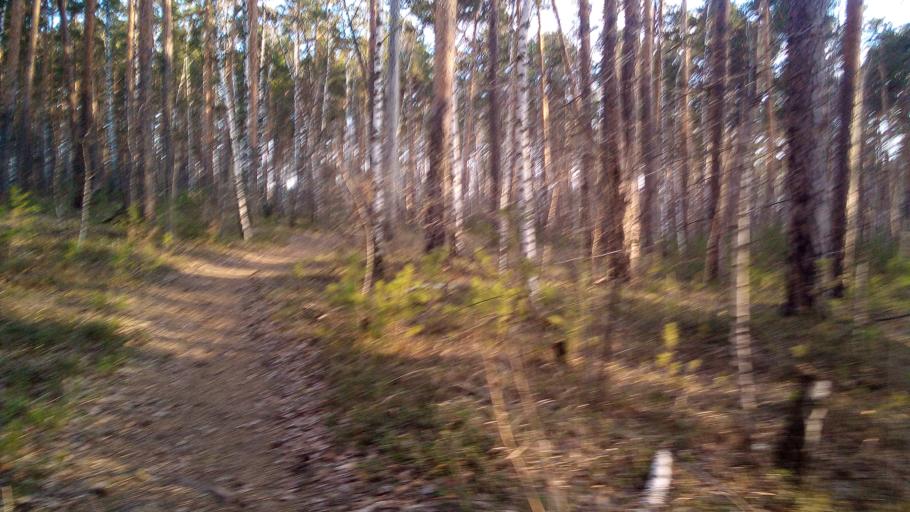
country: RU
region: Chelyabinsk
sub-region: Gorod Chelyabinsk
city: Chelyabinsk
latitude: 55.1614
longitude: 61.3230
